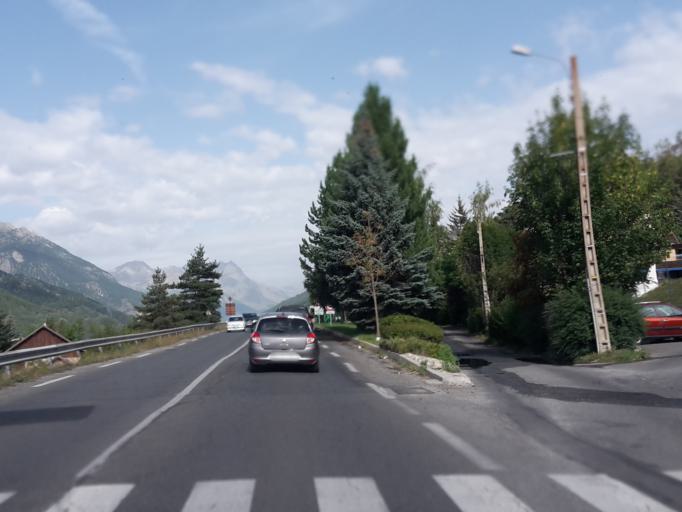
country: FR
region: Provence-Alpes-Cote d'Azur
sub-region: Departement des Hautes-Alpes
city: Saint-Chaffrey
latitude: 44.9180
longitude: 6.6212
